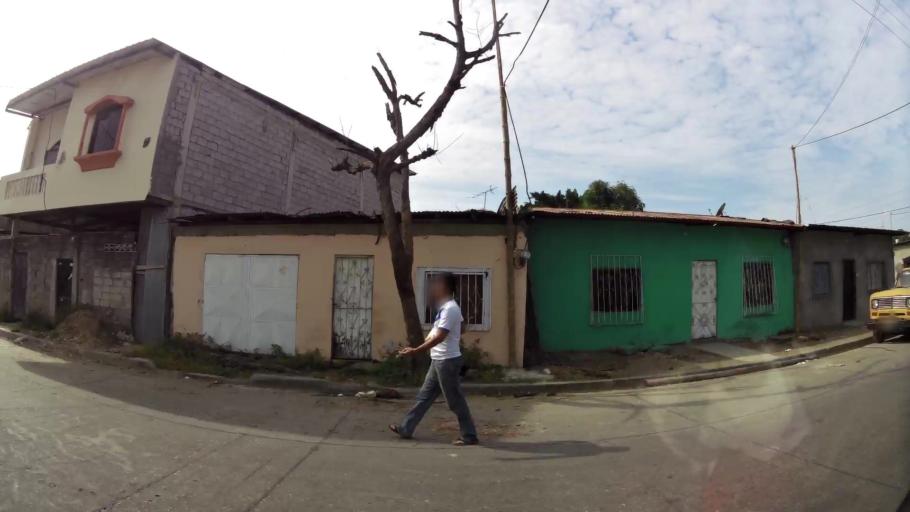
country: EC
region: Guayas
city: Guayaquil
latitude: -2.2577
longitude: -79.8721
